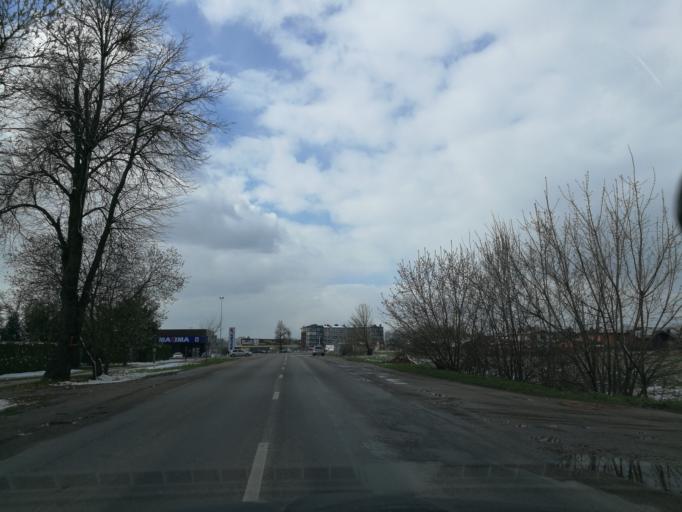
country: LT
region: Kauno apskritis
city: Dainava (Kaunas)
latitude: 54.8533
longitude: 24.0177
